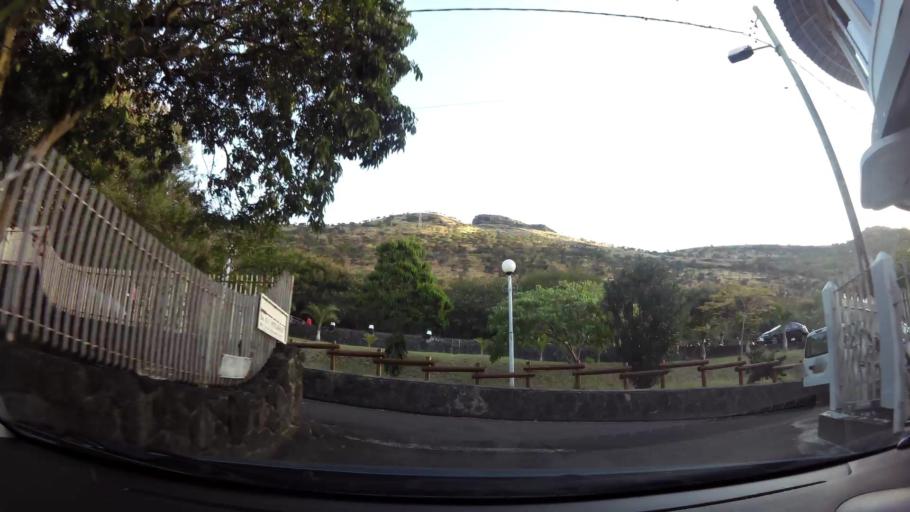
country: MU
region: Port Louis
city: Port Louis
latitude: -20.1747
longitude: 57.5009
